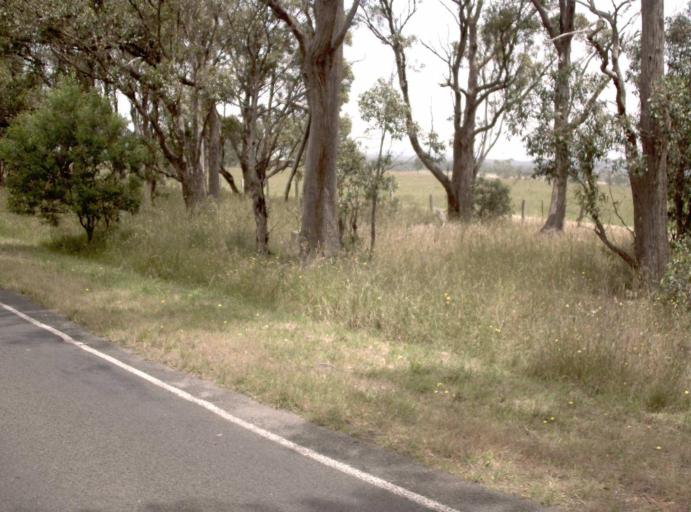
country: AU
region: Victoria
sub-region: Latrobe
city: Traralgon
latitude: -38.4847
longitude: 146.7146
